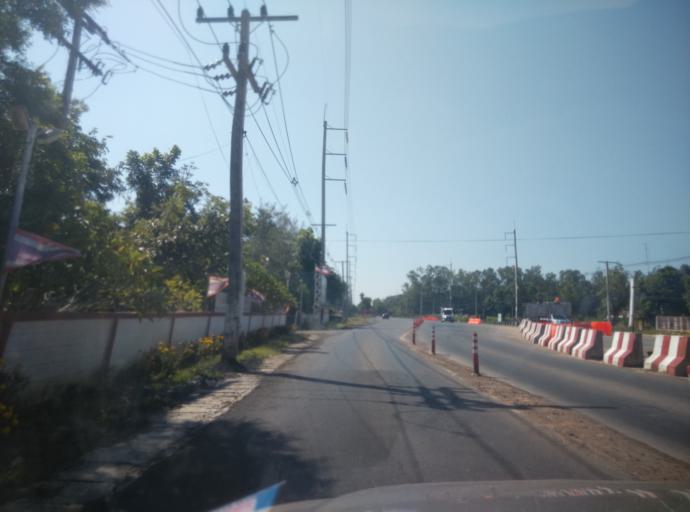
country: TH
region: Sisaket
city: Si Sa Ket
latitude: 15.1188
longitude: 104.2847
